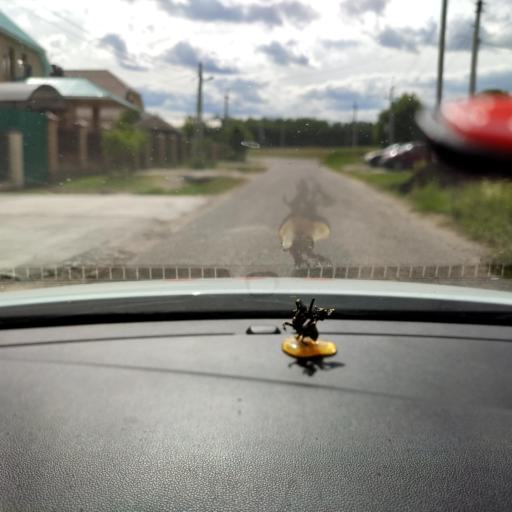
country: RU
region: Tatarstan
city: Stolbishchi
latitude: 55.6331
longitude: 49.1355
